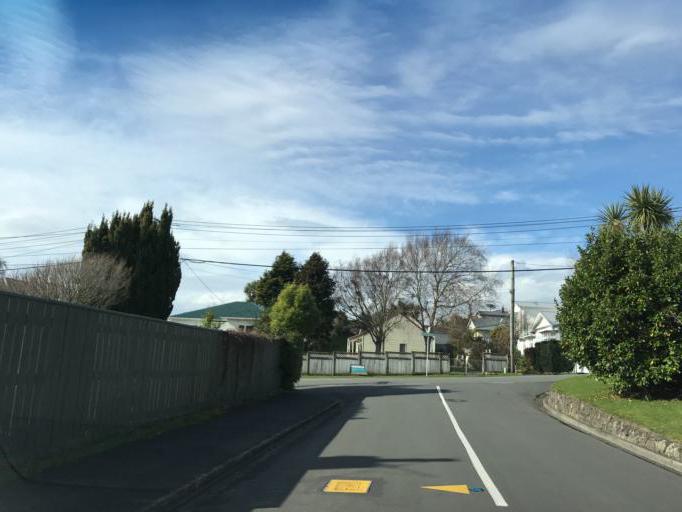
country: NZ
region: Wellington
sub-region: Wellington City
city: Kelburn
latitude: -41.2874
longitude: 174.7355
